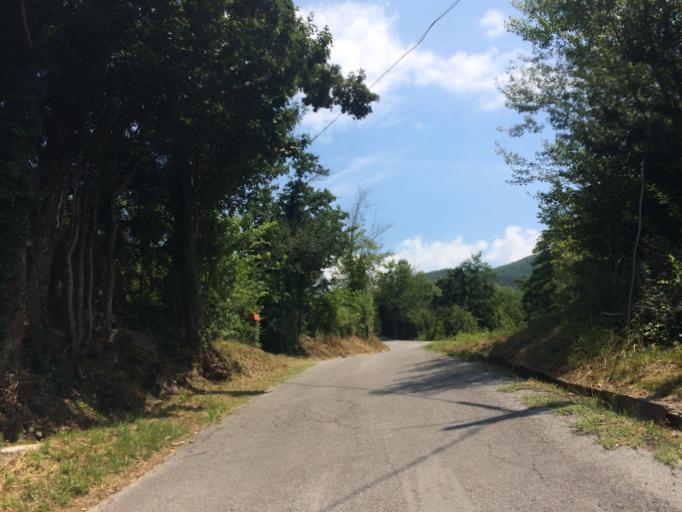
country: IT
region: Piedmont
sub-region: Provincia di Cuneo
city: Bagnasco
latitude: 44.3131
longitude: 8.0598
